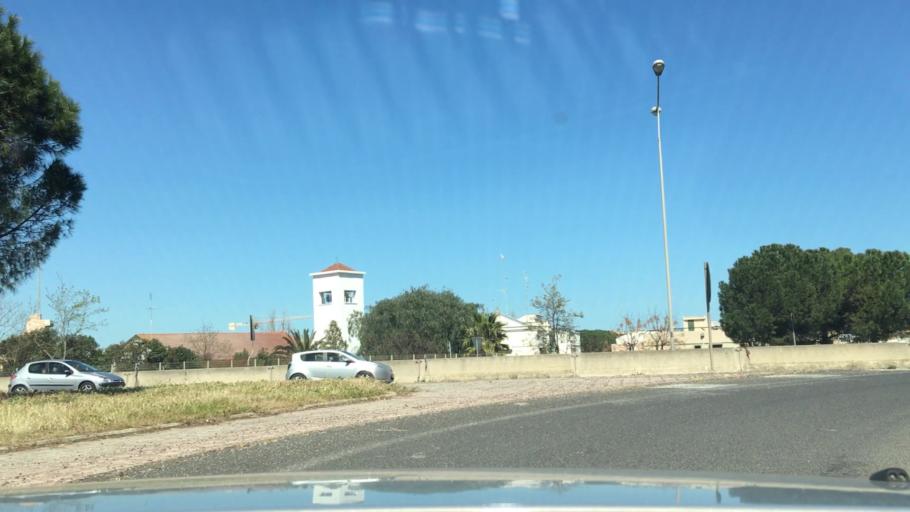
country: IT
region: Apulia
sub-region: Provincia di Bari
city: Triggiano
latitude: 41.0895
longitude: 16.8912
